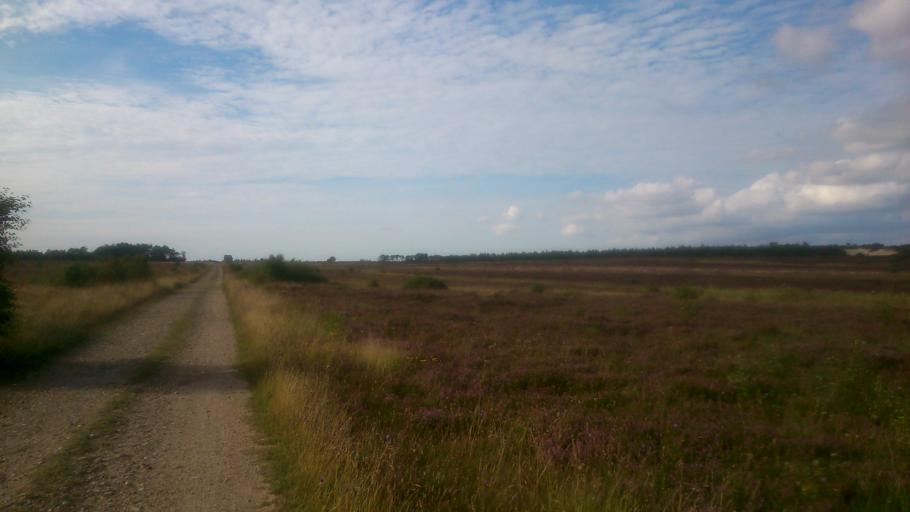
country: DK
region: Central Jutland
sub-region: Ringkobing-Skjern Kommune
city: Skjern
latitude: 56.0242
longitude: 8.4505
